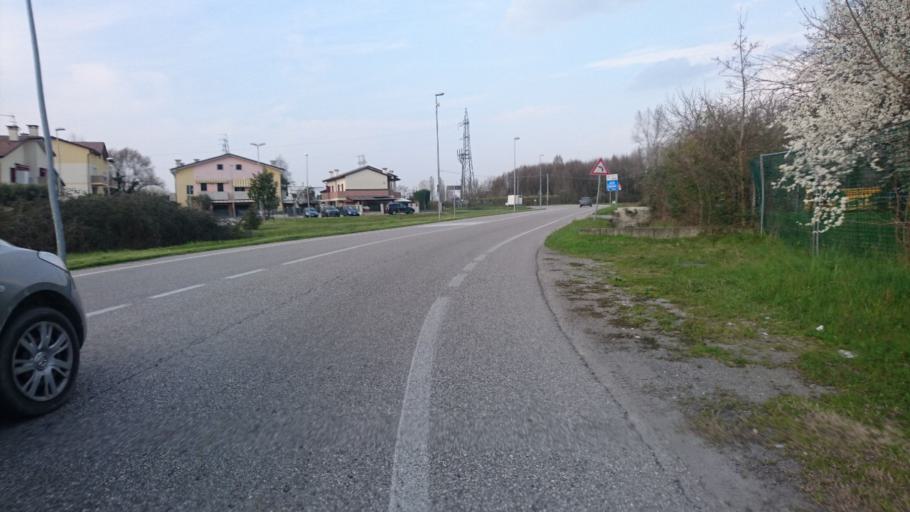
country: IT
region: Veneto
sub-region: Provincia di Padova
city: San Biagio
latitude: 45.3724
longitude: 11.7323
